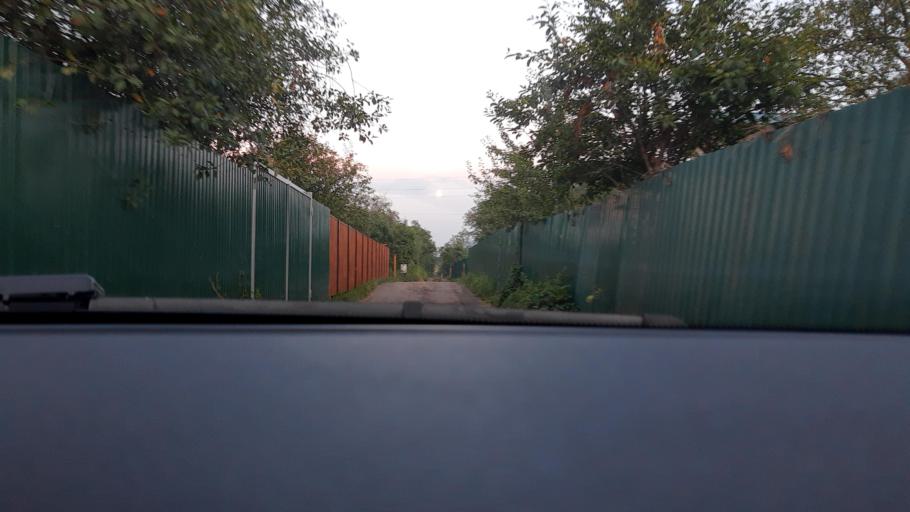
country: RU
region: Nizjnij Novgorod
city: Kstovo
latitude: 56.1557
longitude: 44.2565
